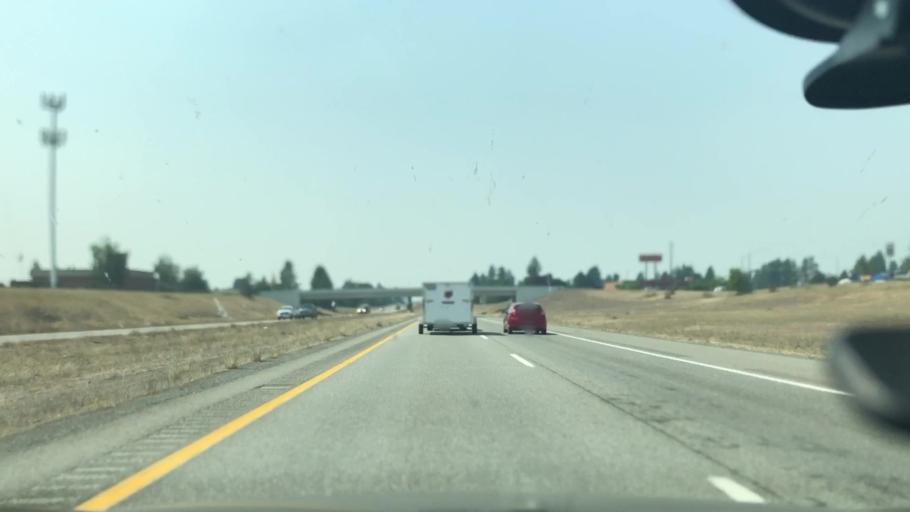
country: US
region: Idaho
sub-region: Kootenai County
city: Post Falls
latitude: 47.7127
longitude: -116.9338
